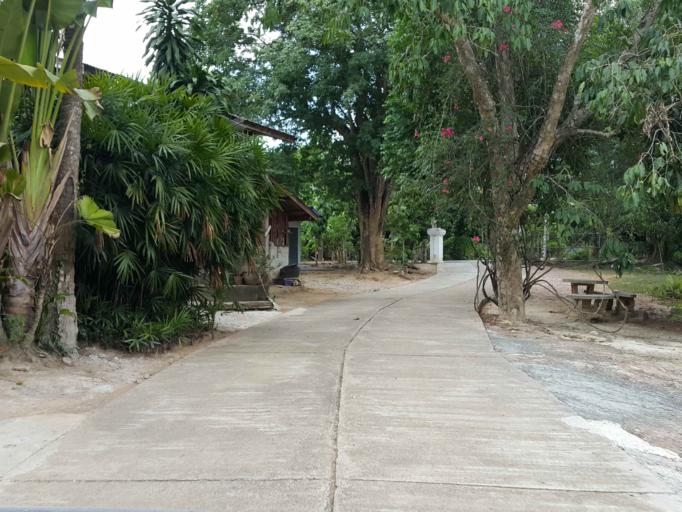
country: TH
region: Chiang Mai
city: Hang Dong
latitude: 18.7600
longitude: 98.9076
